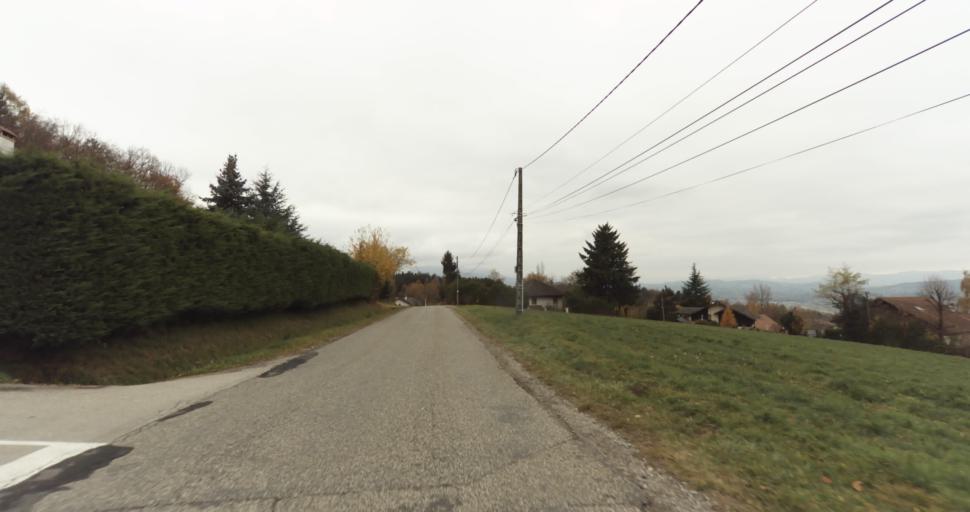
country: FR
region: Rhone-Alpes
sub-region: Departement de la Haute-Savoie
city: Saint-Martin-Bellevue
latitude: 45.9558
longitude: 6.1444
